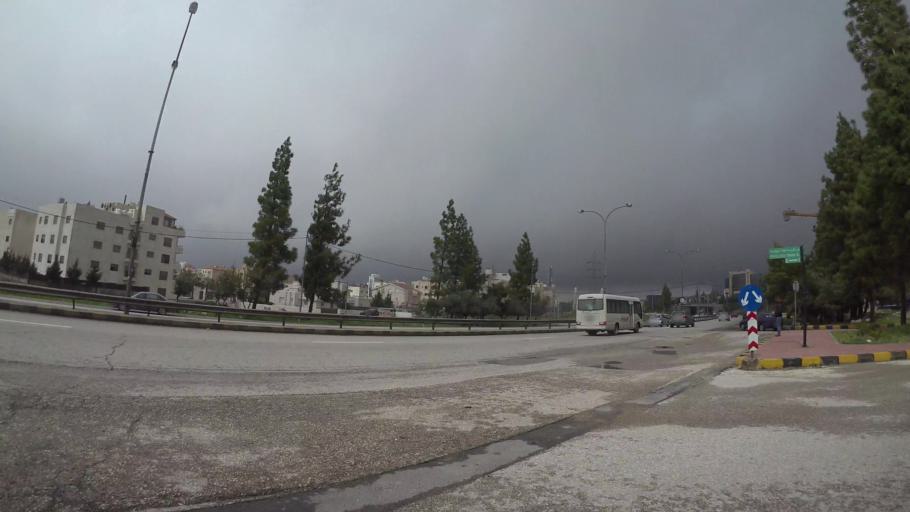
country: JO
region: Amman
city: Wadi as Sir
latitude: 31.9429
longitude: 35.8583
